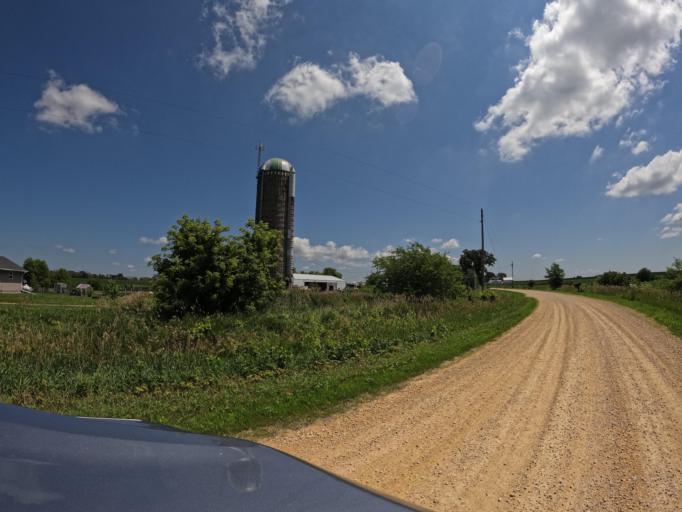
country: US
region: Iowa
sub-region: Clinton County
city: De Witt
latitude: 41.7784
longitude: -90.4237
